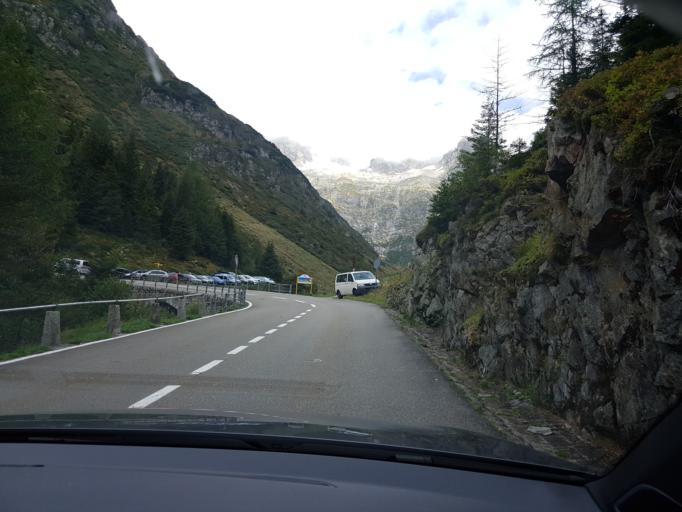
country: CH
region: Obwalden
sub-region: Obwalden
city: Engelberg
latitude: 46.7433
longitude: 8.5089
